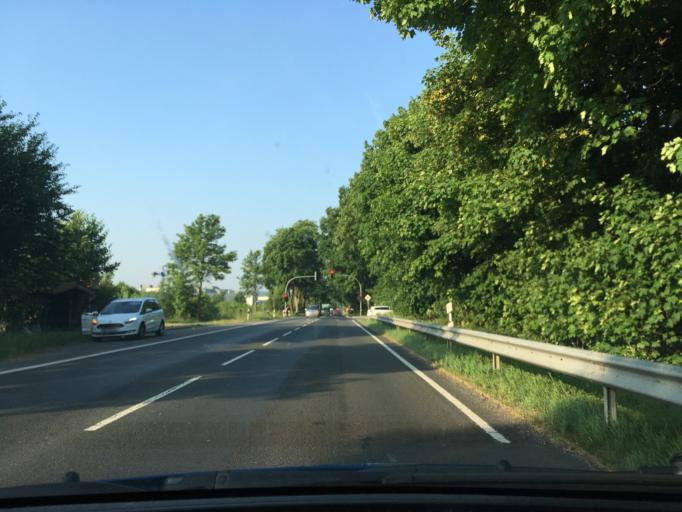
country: DE
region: Lower Saxony
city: Buchholz in der Nordheide
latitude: 53.3564
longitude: 9.8642
